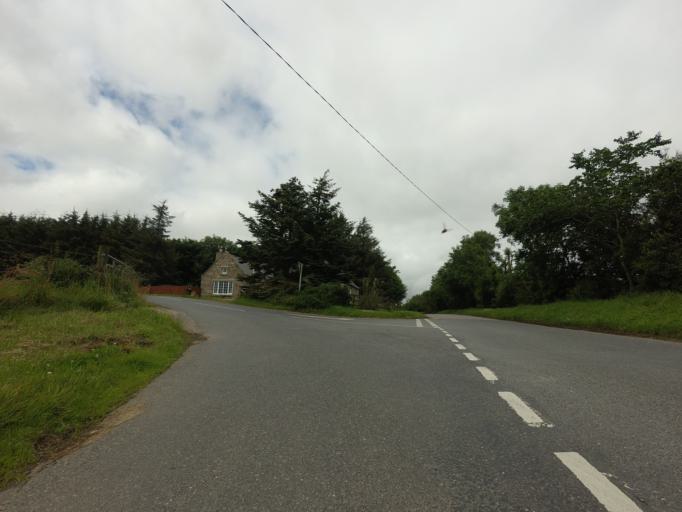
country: GB
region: Scotland
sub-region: Aberdeenshire
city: Rosehearty
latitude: 57.5395
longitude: -2.1885
